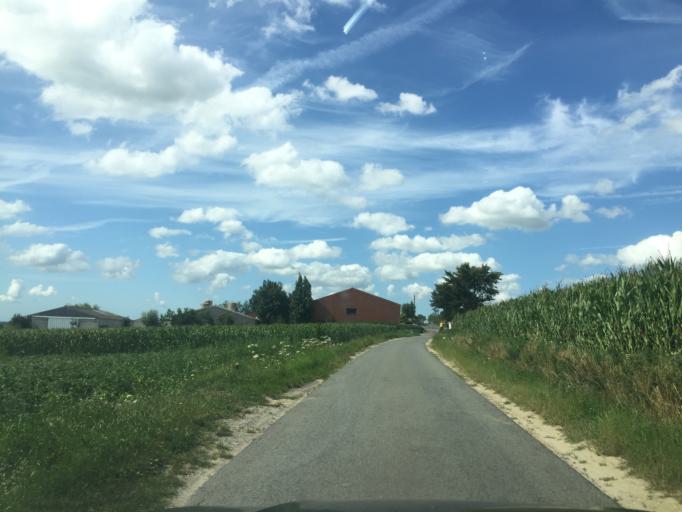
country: BE
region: Flanders
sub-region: Provincie West-Vlaanderen
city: Staden
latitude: 50.9438
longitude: 3.0117
